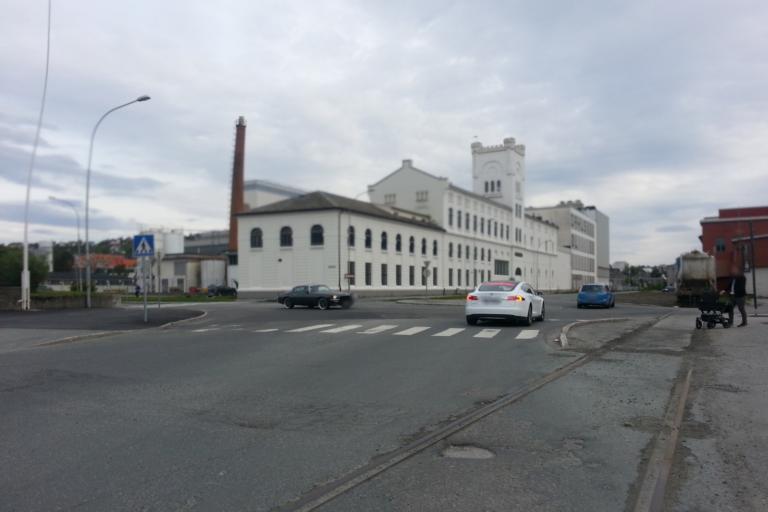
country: NO
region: Sor-Trondelag
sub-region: Trondheim
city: Trondheim
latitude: 63.4425
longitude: 10.4271
